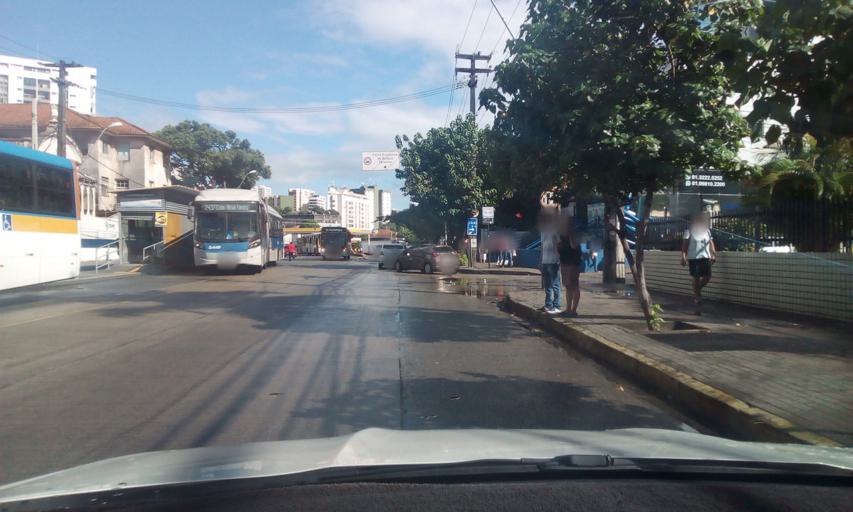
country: BR
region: Pernambuco
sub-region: Recife
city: Recife
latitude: -8.0562
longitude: -34.8938
